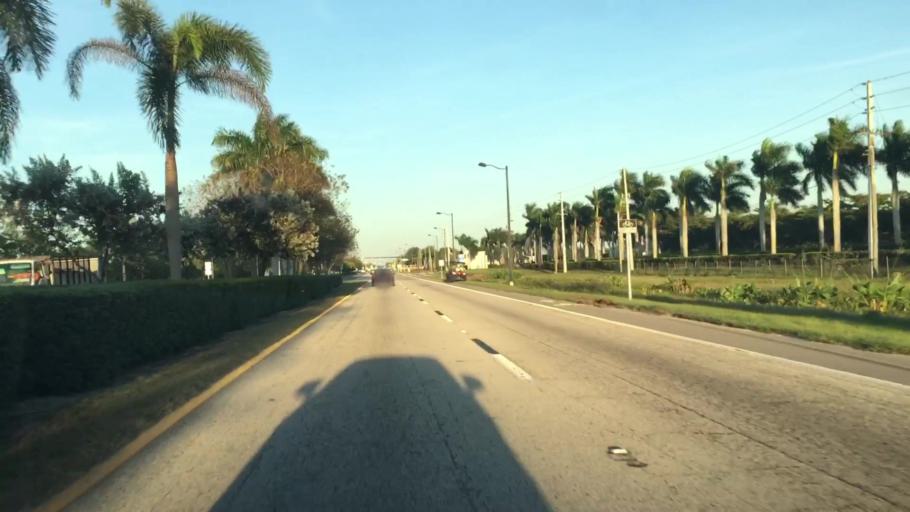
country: US
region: Florida
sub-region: Lee County
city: Estero
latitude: 26.4335
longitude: -81.7754
